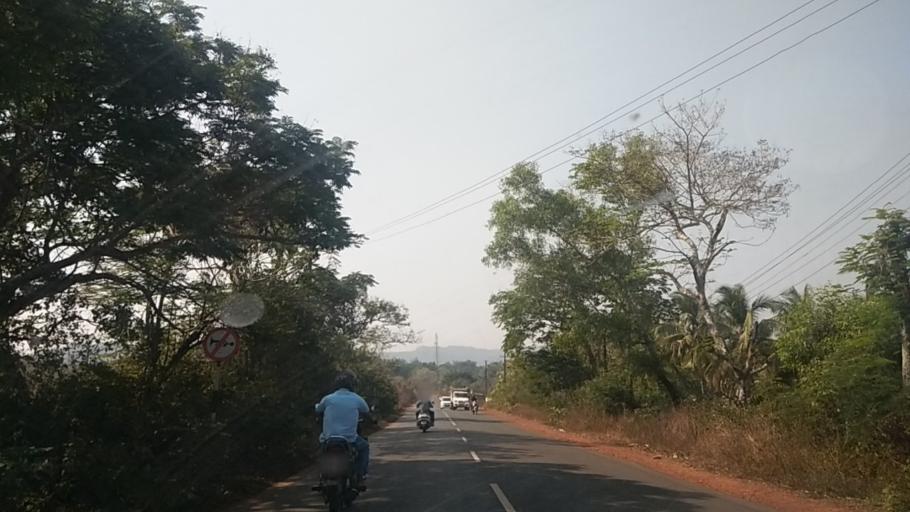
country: IN
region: Goa
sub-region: North Goa
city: Dicholi
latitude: 15.5824
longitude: 73.9661
